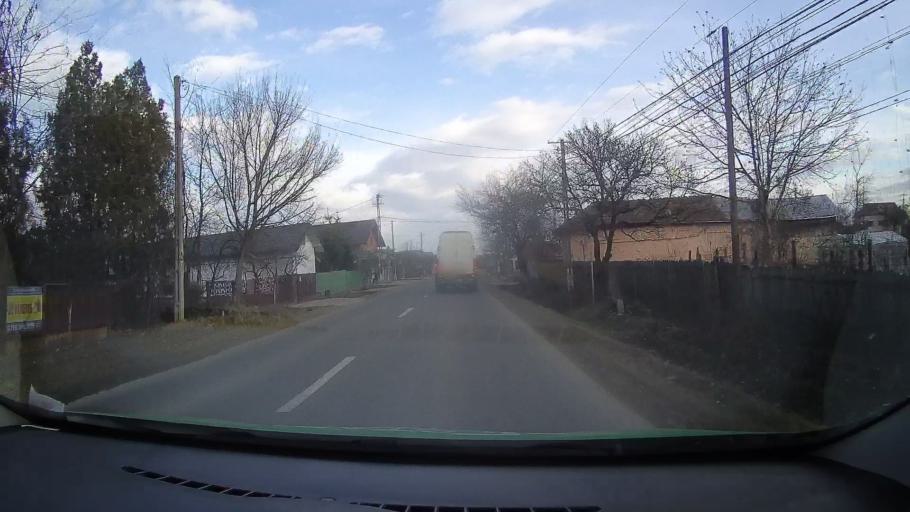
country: RO
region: Dambovita
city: Razvad
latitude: 44.9335
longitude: 25.5421
